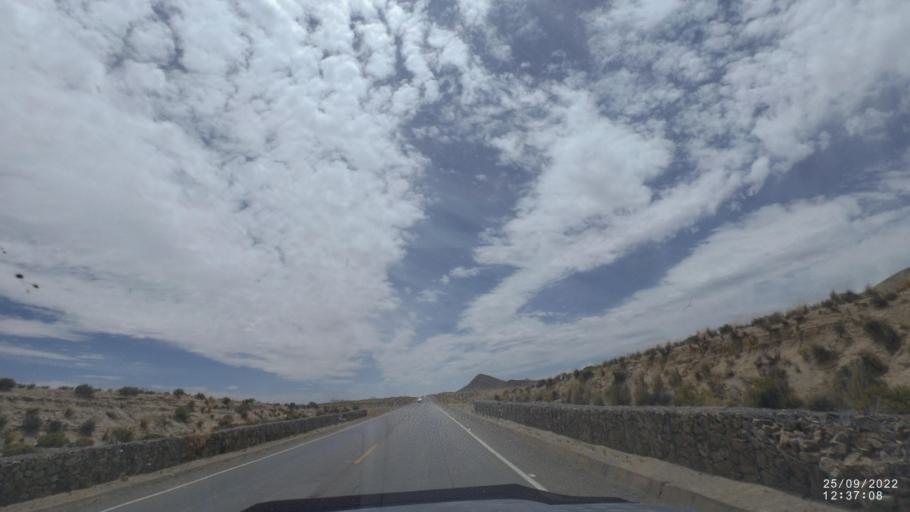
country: BO
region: Oruro
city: Machacamarca
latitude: -18.1527
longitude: -66.9877
